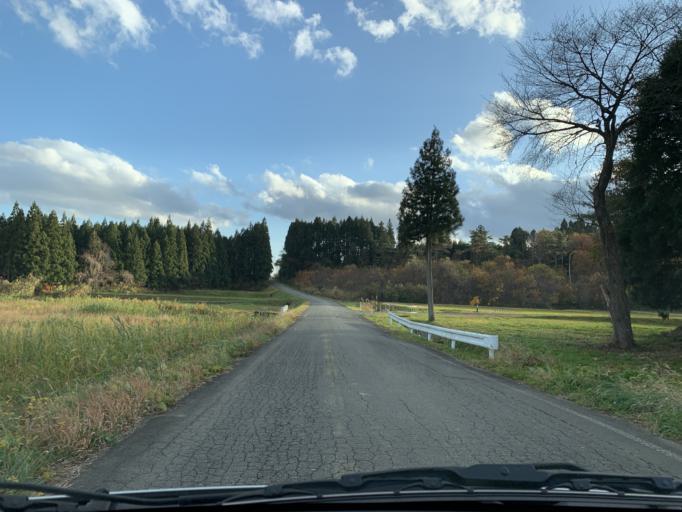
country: JP
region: Iwate
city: Mizusawa
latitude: 39.1145
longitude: 141.0001
